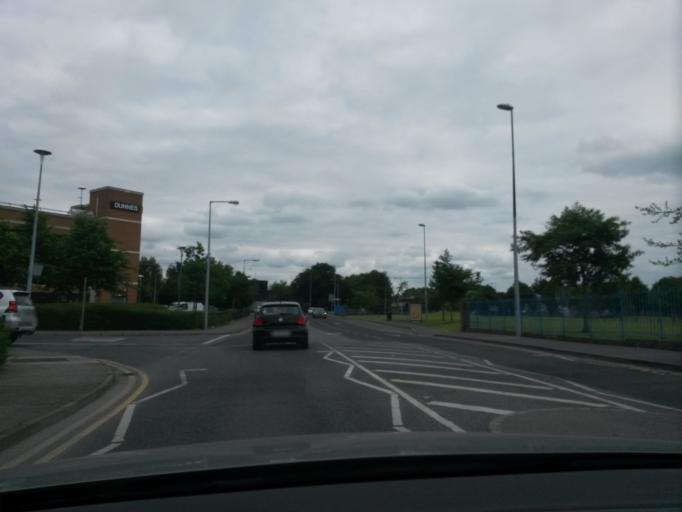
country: IE
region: Munster
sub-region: An Clar
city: Ennis
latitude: 52.8427
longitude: -8.9786
